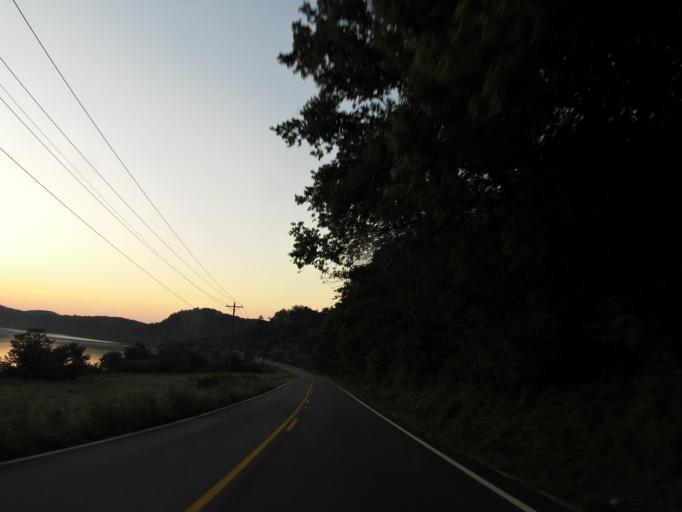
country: US
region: Tennessee
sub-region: Loudon County
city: Greenback
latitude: 35.5474
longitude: -84.0881
